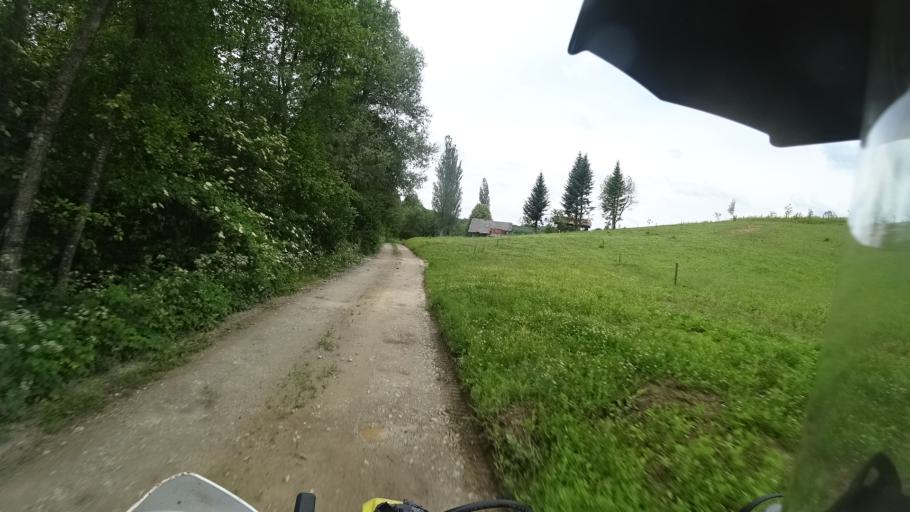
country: HR
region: Karlovacka
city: Vojnic
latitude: 45.2476
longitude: 15.6692
